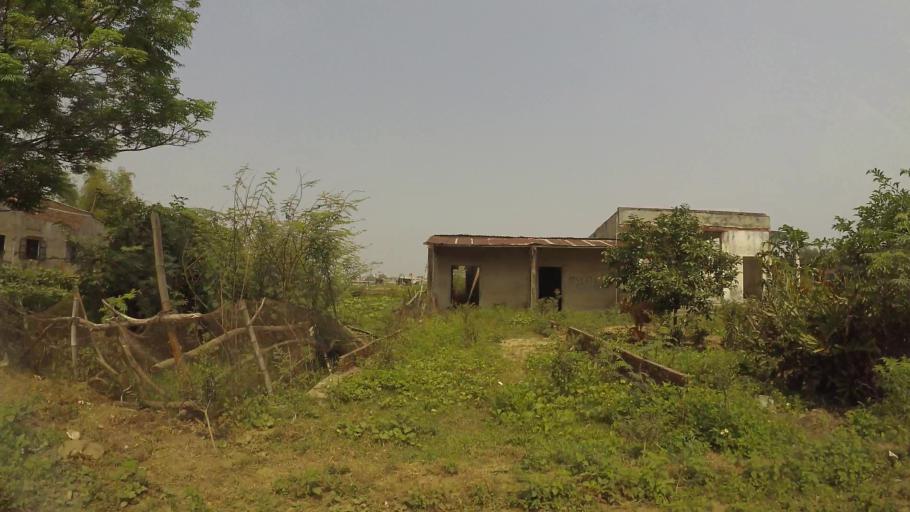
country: VN
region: Da Nang
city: Ngu Hanh Son
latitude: 16.0159
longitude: 108.2478
